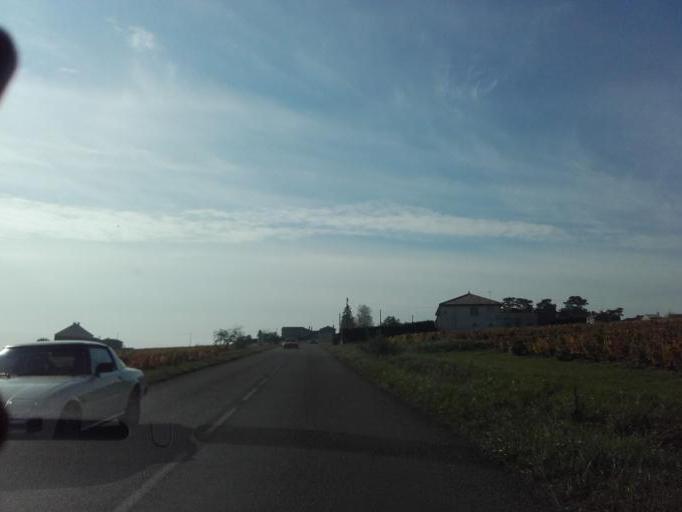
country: FR
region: Bourgogne
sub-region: Departement de Saone-et-Loire
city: Creches-sur-Saone
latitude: 46.2445
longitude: 4.7535
